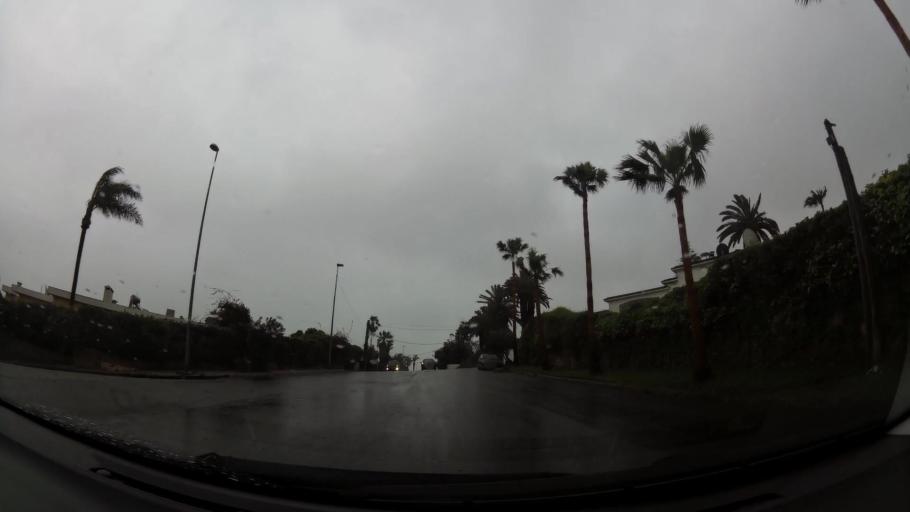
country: MA
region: Grand Casablanca
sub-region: Casablanca
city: Casablanca
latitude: 33.5925
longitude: -7.6639
